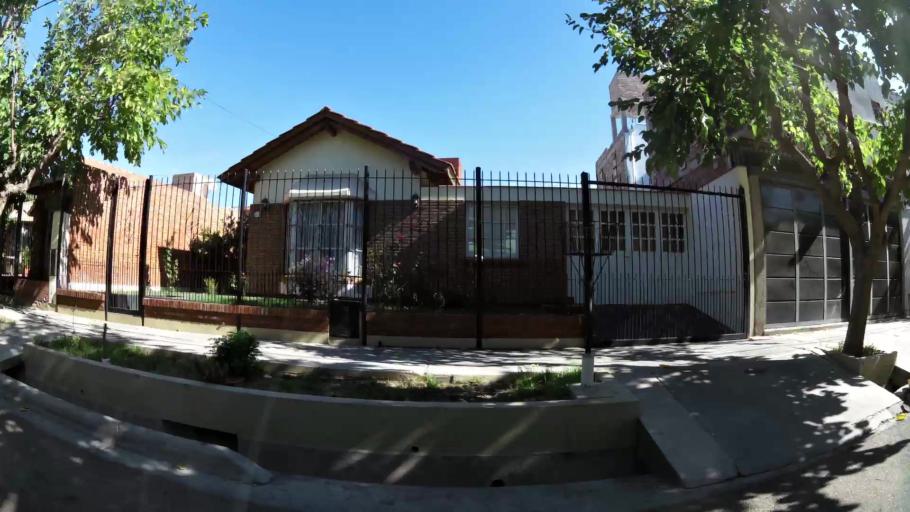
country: AR
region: Mendoza
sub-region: Departamento de Godoy Cruz
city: Godoy Cruz
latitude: -32.9422
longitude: -68.8056
